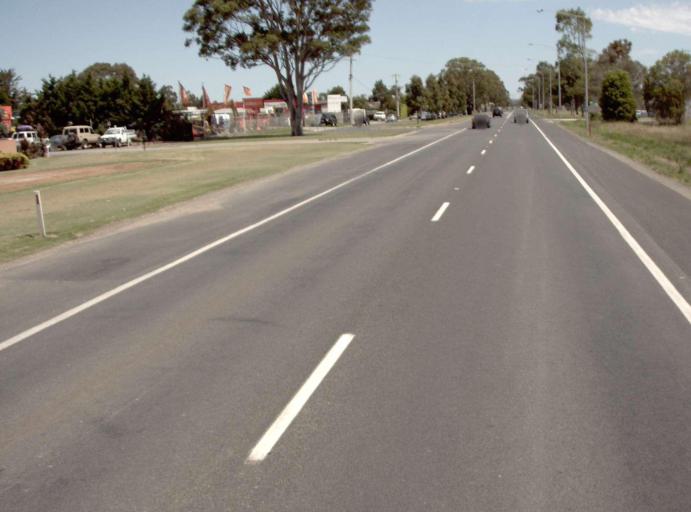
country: AU
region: Victoria
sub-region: Wellington
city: Sale
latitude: -38.0863
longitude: 147.0703
